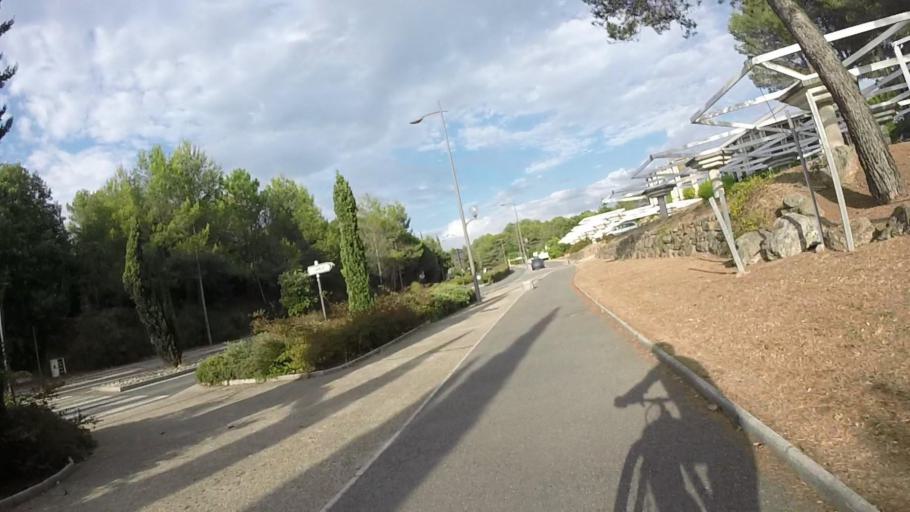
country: FR
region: Provence-Alpes-Cote d'Azur
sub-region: Departement des Alpes-Maritimes
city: Biot
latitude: 43.6161
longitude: 7.0663
